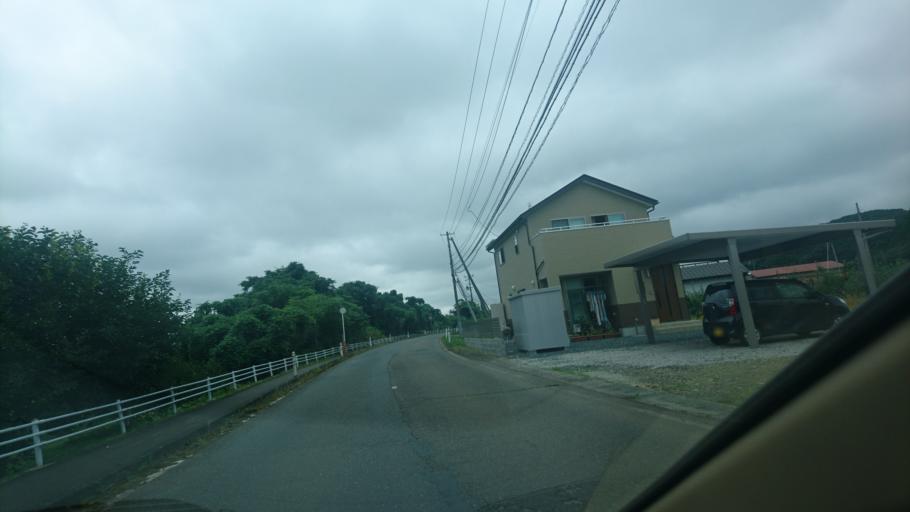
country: JP
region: Iwate
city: Kitakami
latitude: 39.2464
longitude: 141.1205
